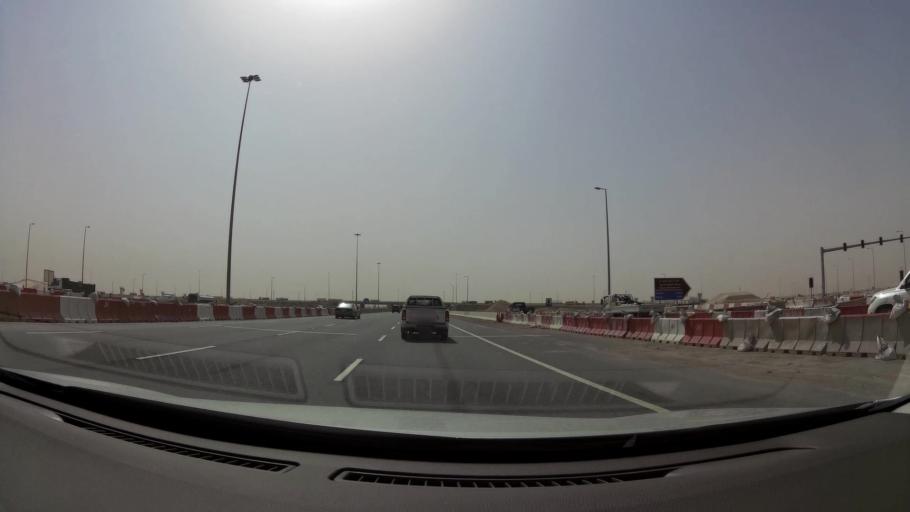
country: QA
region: Baladiyat ar Rayyan
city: Ar Rayyan
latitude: 25.1744
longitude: 51.3313
